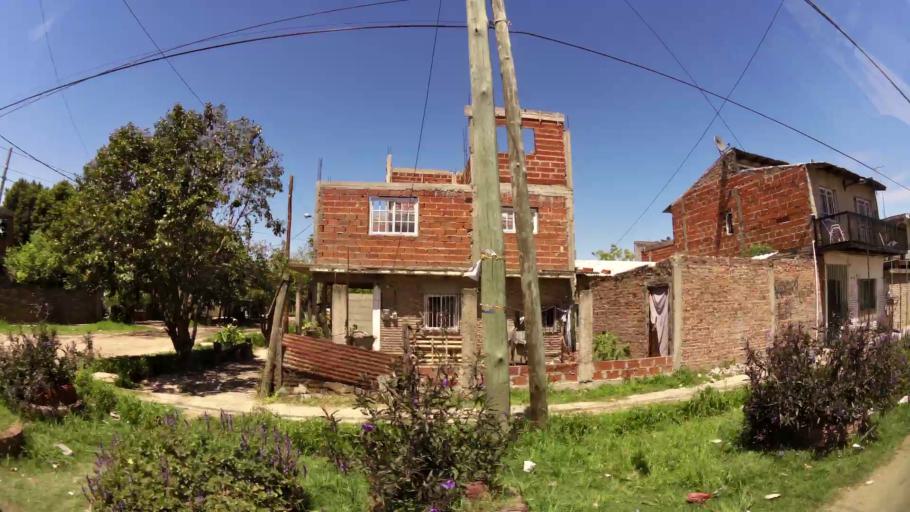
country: AR
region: Buenos Aires
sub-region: Partido de Quilmes
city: Quilmes
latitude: -34.7220
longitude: -58.3230
